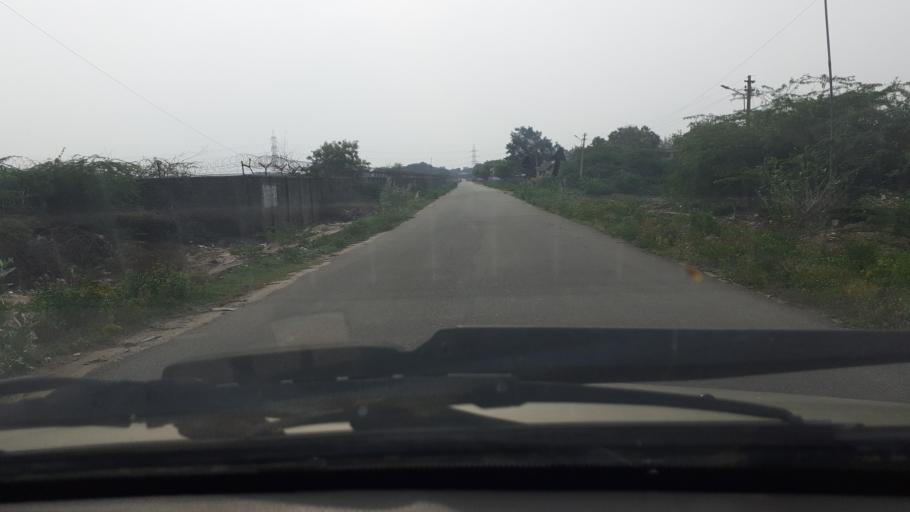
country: IN
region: Tamil Nadu
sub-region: Thoothukkudi
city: Korampallam
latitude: 8.7933
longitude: 78.1086
